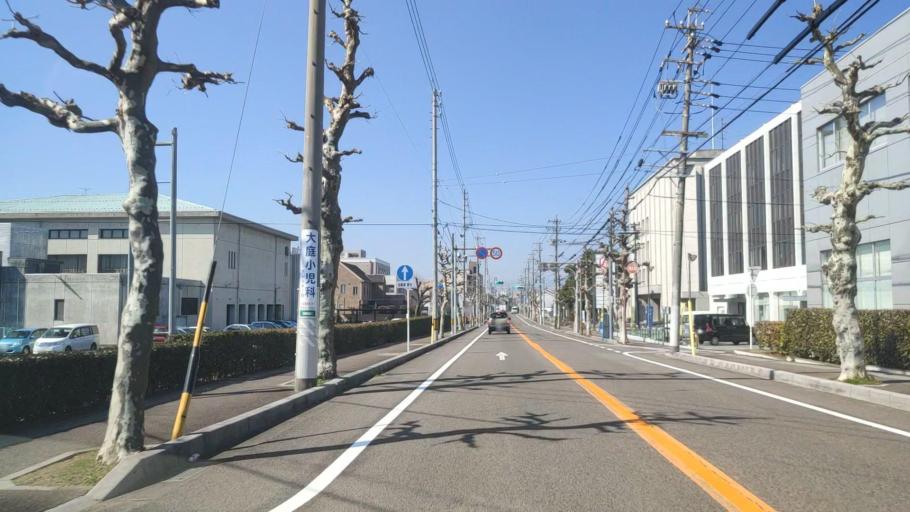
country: JP
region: Gifu
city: Gifu-shi
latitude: 35.3979
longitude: 136.7617
